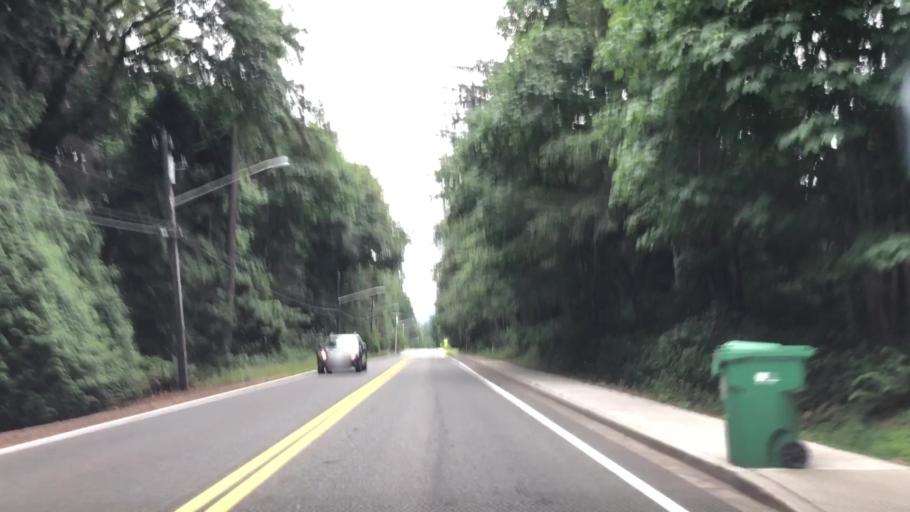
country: US
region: Washington
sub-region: King County
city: Woodinville
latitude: 47.7882
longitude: -122.1569
